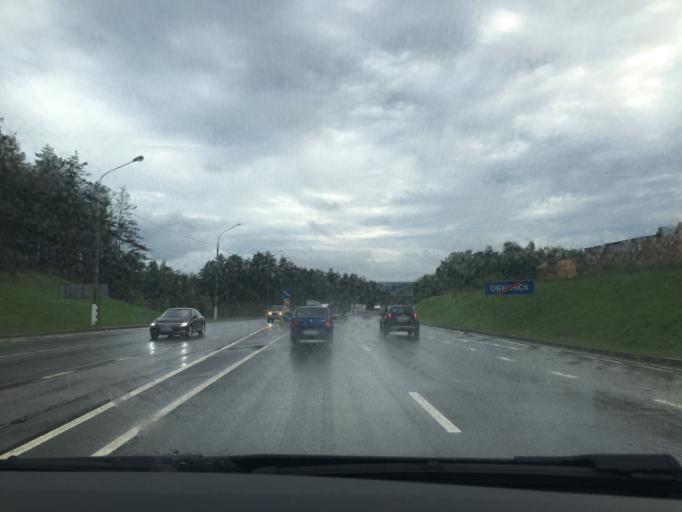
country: RU
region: Kaluga
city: Obninsk
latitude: 55.0561
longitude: 36.6183
